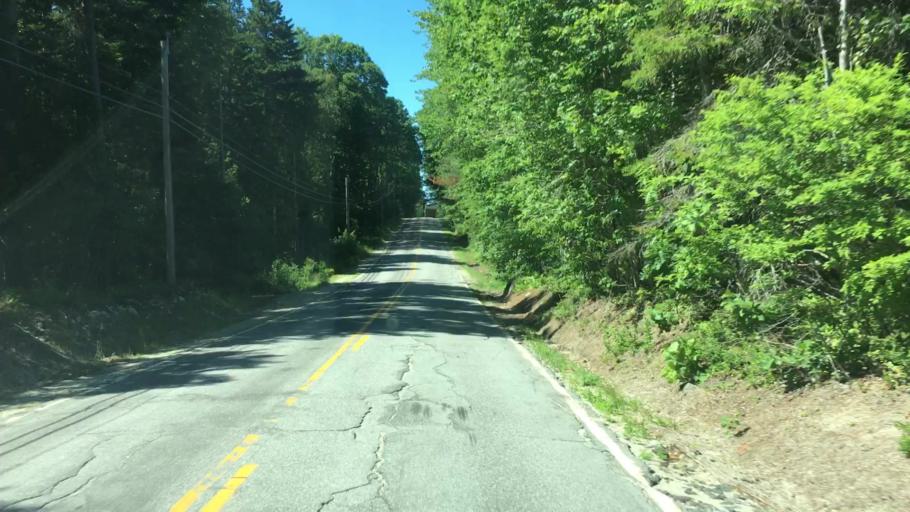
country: US
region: Maine
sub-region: Hancock County
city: Sedgwick
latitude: 44.3218
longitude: -68.6087
